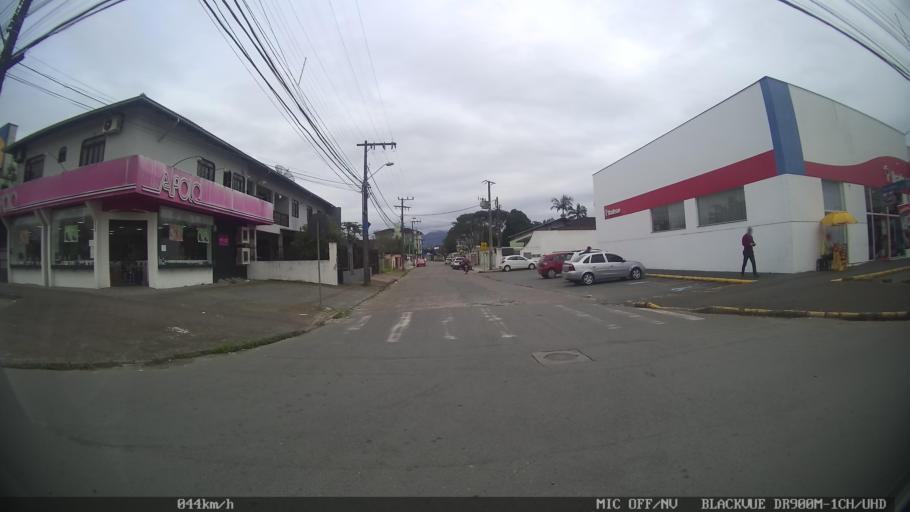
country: BR
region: Santa Catarina
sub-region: Joinville
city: Joinville
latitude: -26.2680
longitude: -48.8723
